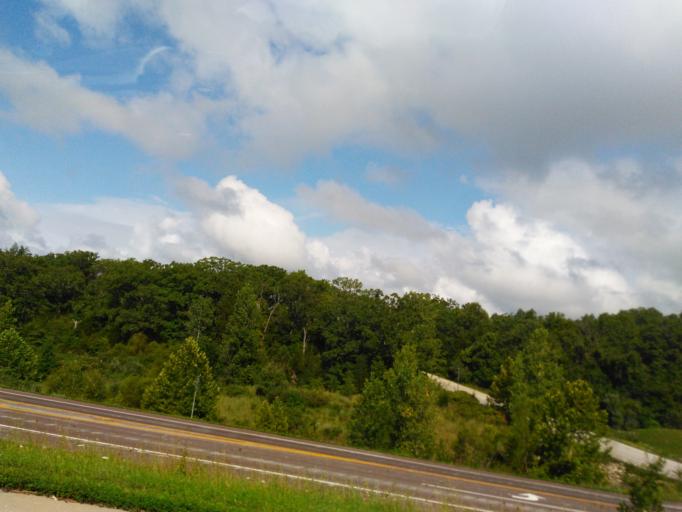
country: US
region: Missouri
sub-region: Jefferson County
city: Hillsboro
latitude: 38.2569
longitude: -90.5554
